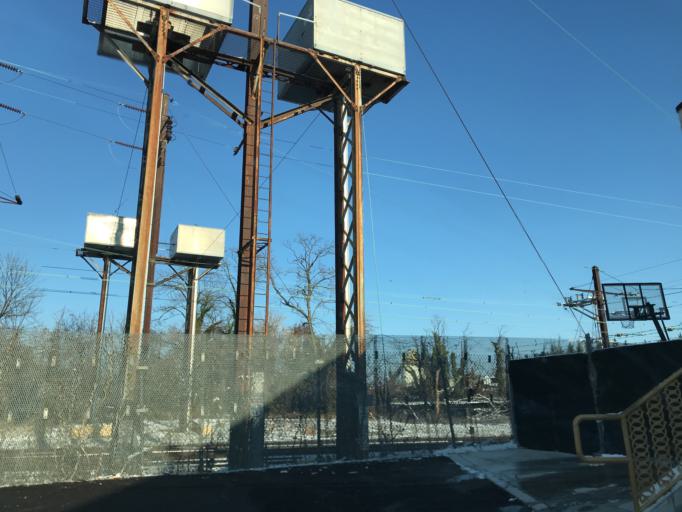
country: US
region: Maryland
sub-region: City of Baltimore
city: Baltimore
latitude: 39.3018
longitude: -76.6485
